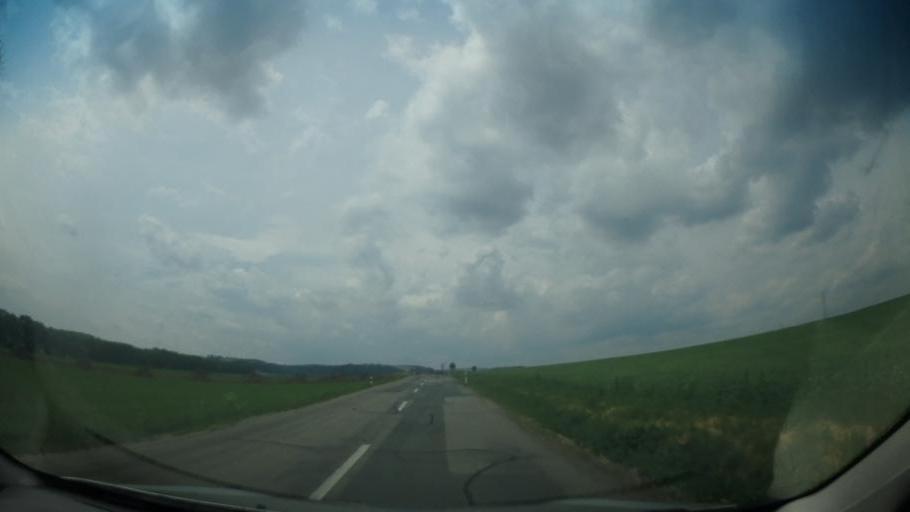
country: CZ
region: South Moravian
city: Boritov
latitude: 49.4328
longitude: 16.5727
